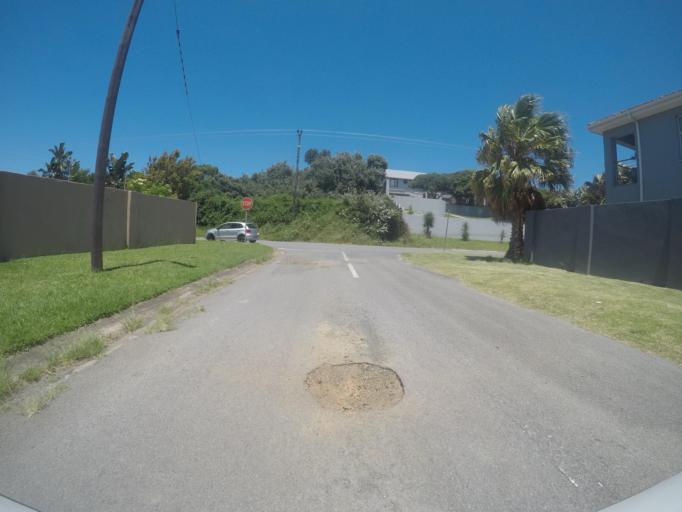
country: ZA
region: Eastern Cape
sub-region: Buffalo City Metropolitan Municipality
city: East London
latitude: -32.9492
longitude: 28.0164
